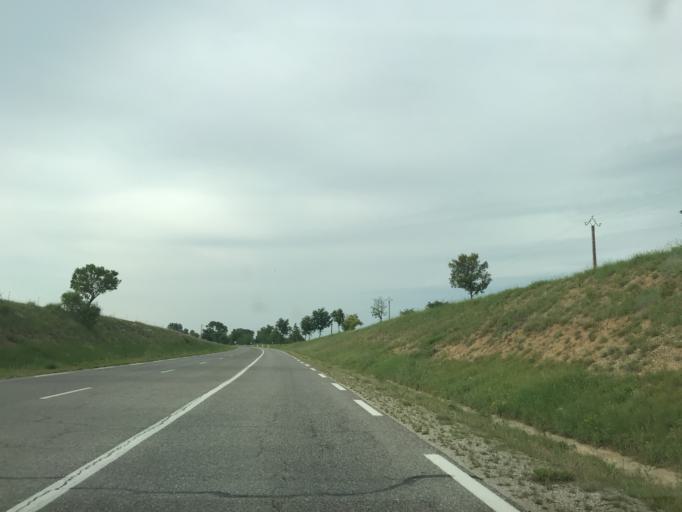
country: FR
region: Provence-Alpes-Cote d'Azur
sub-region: Departement des Alpes-de-Haute-Provence
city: Oraison
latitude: 43.9461
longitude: 5.8890
